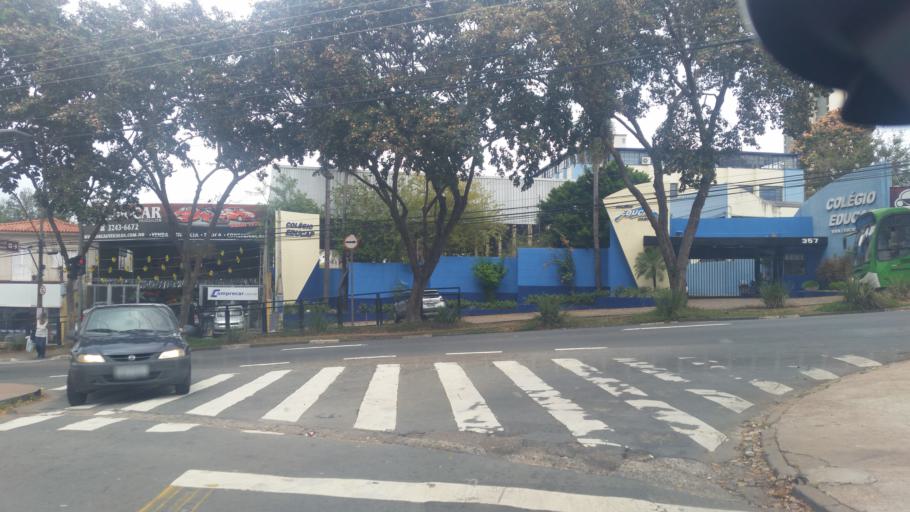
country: BR
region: Sao Paulo
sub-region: Campinas
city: Campinas
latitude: -22.8812
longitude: -47.0693
